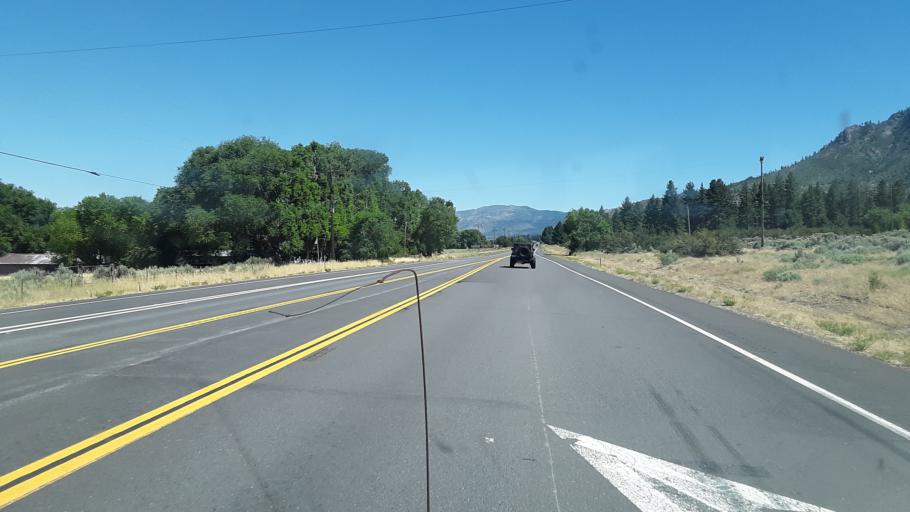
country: US
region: California
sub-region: Lassen County
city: Janesville
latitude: 40.2464
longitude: -120.4584
